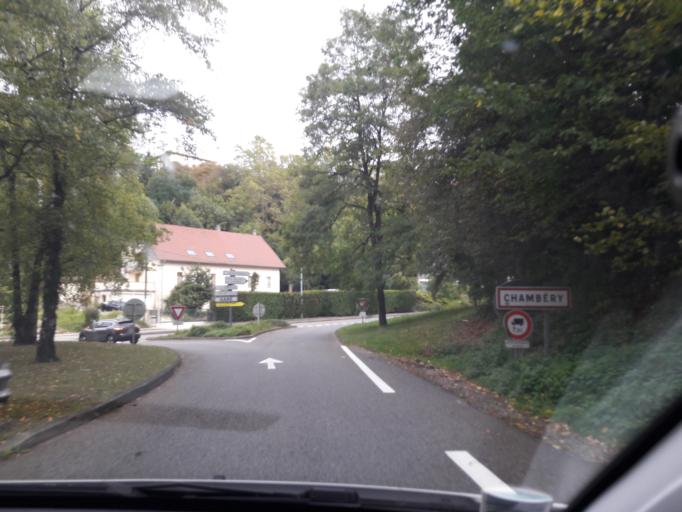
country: FR
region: Rhone-Alpes
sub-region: Departement de la Savoie
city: Chambery
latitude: 45.5789
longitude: 5.9188
